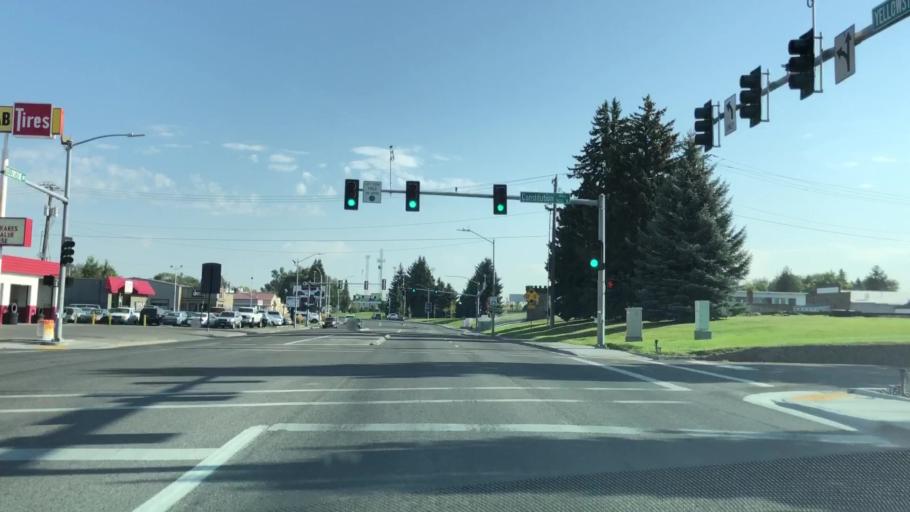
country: US
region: Idaho
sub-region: Bonneville County
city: Idaho Falls
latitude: 43.4932
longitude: -112.0373
